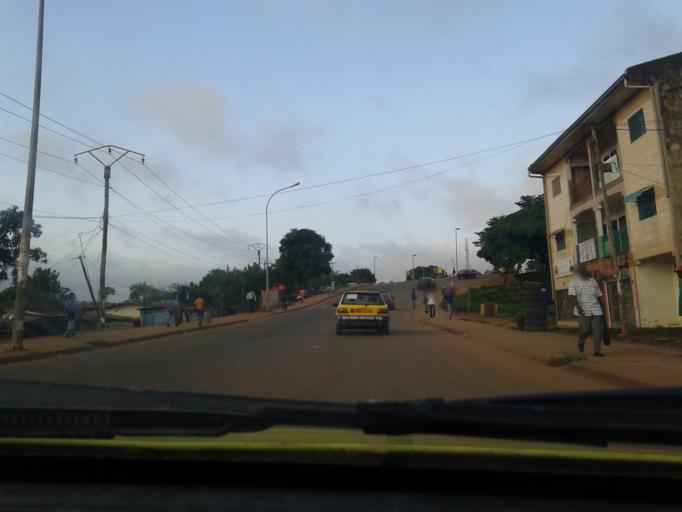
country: CM
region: Centre
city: Yaounde
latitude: 3.9027
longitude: 11.5257
